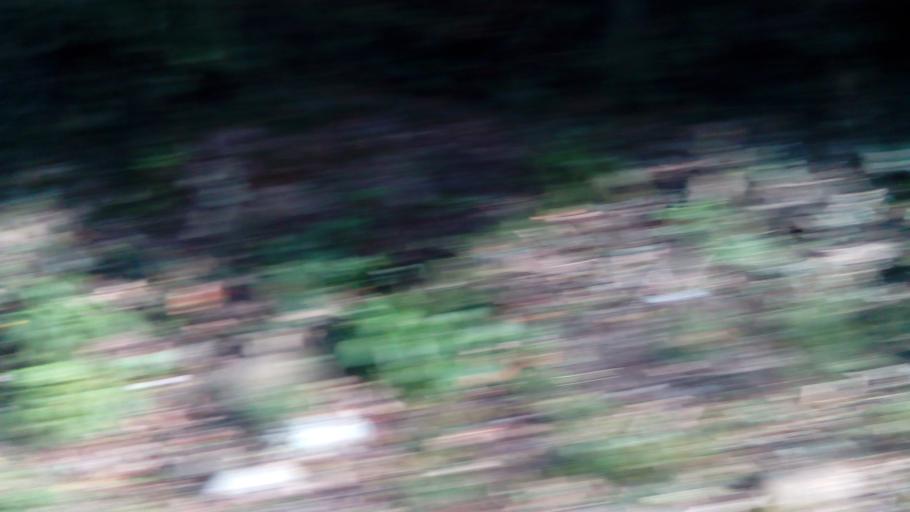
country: TW
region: Taiwan
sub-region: Hualien
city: Hualian
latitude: 24.3490
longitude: 121.3217
